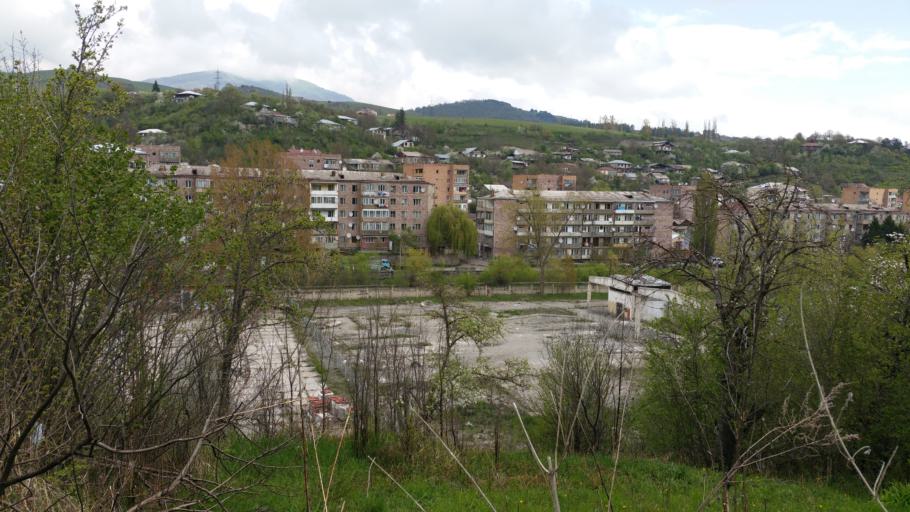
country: AM
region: Tavush
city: Dilijan
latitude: 40.7386
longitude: 44.8428
